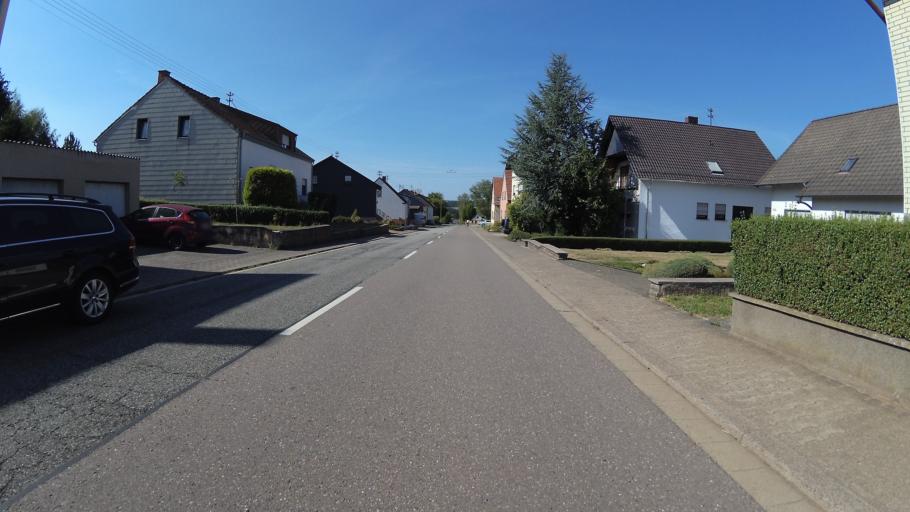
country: DE
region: Saarland
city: Eppelborn
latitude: 49.3660
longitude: 6.9833
